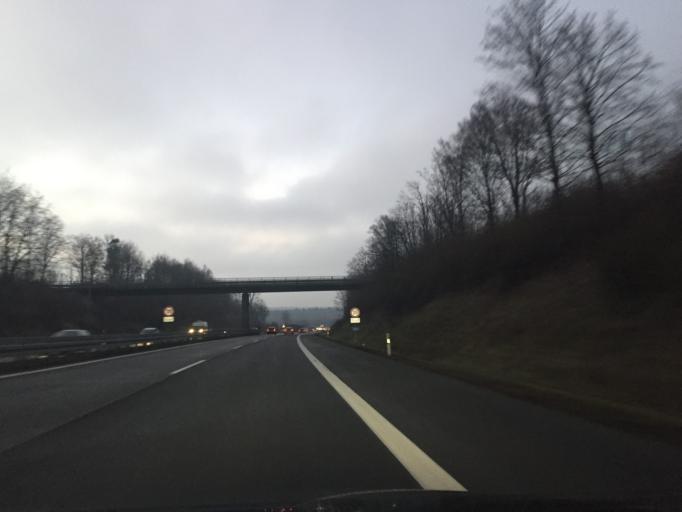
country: DE
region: Bavaria
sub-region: Upper Bavaria
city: Landsberg am Lech
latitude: 48.0601
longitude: 10.8843
